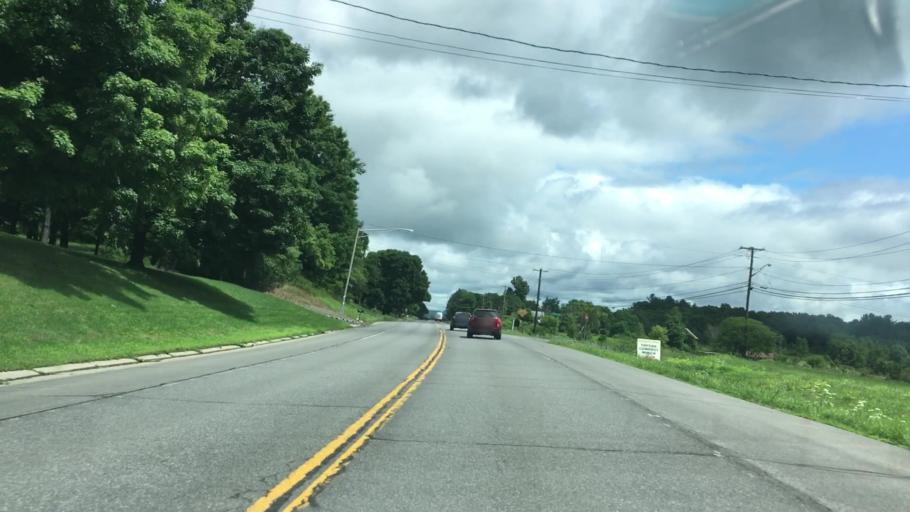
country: US
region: New York
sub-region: Rensselaer County
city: Poestenkill
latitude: 42.8047
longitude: -73.5522
